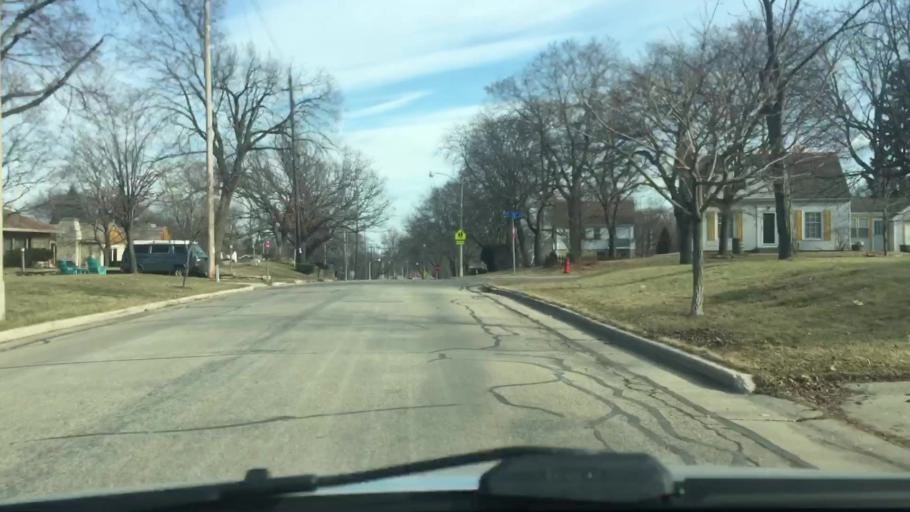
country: US
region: Wisconsin
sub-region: Waukesha County
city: Elm Grove
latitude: 43.0401
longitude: -88.0577
